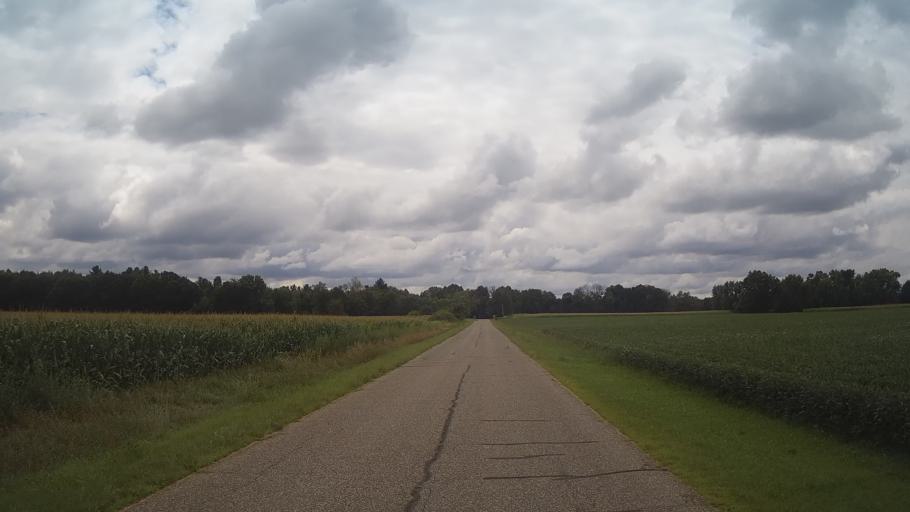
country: US
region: Wisconsin
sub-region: Adams County
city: Friendship
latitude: 44.0283
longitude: -89.9177
